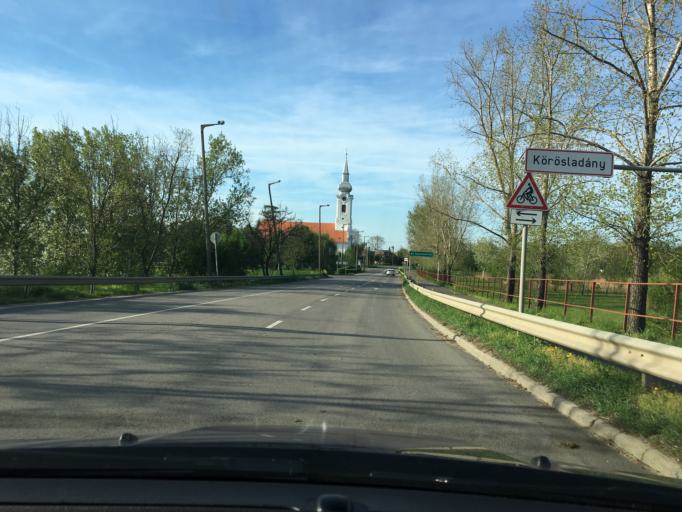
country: HU
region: Bekes
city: Korosladany
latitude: 46.9544
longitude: 21.0819
